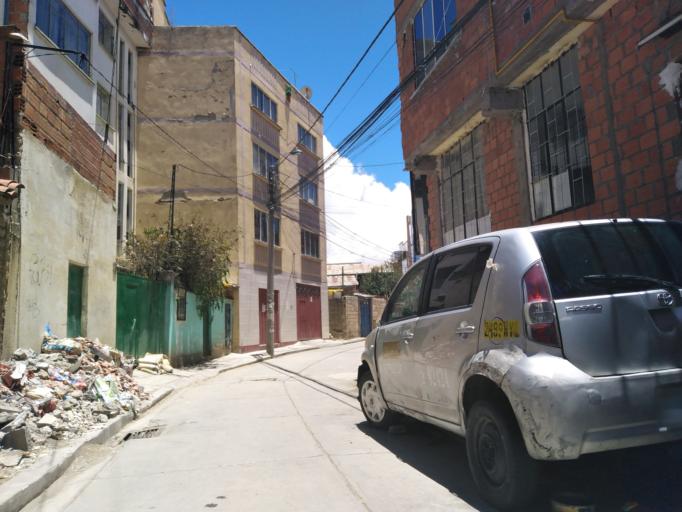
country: BO
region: La Paz
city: La Paz
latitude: -16.5131
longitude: -68.1395
